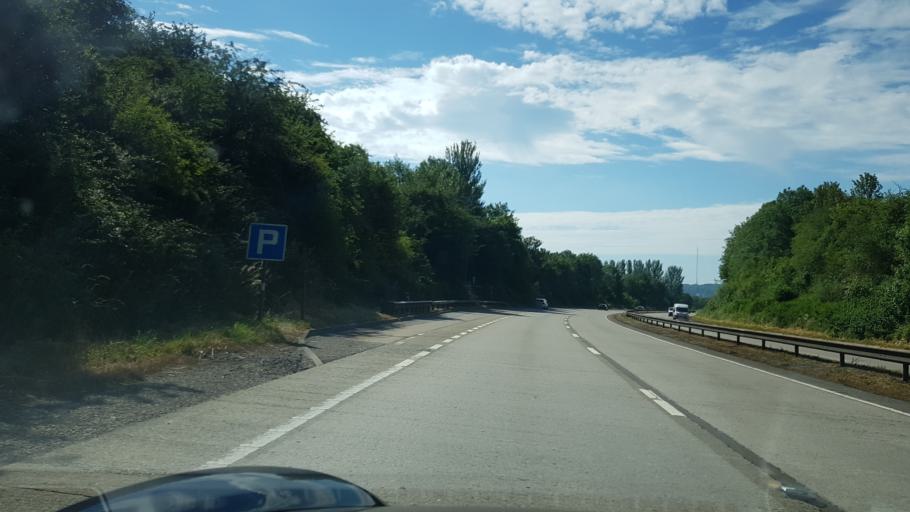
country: GB
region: Wales
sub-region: Cardiff
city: Pentyrch
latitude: 51.4986
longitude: -3.2963
